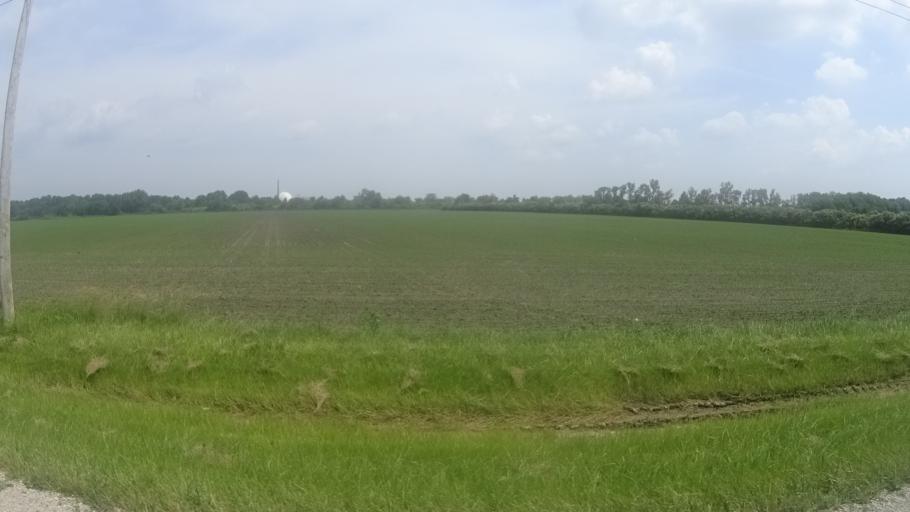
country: US
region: Ohio
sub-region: Erie County
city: Milan
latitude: 41.3358
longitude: -82.6512
